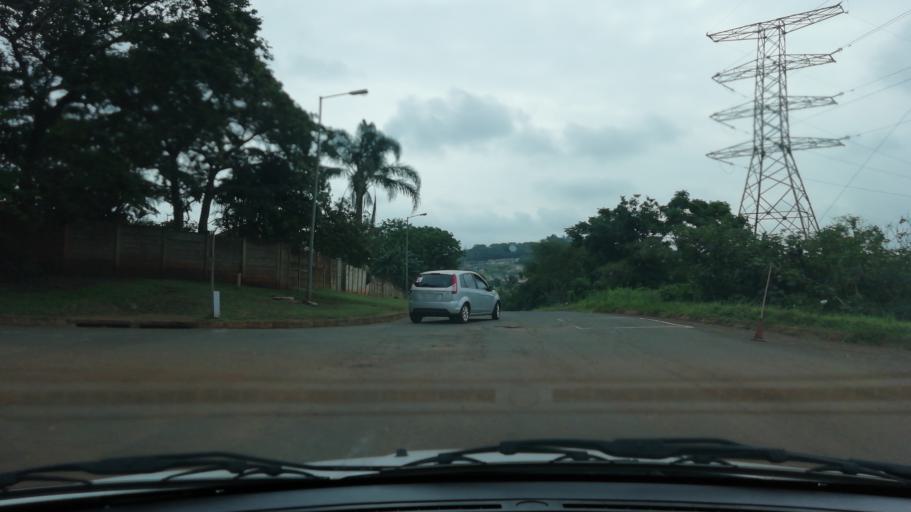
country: ZA
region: KwaZulu-Natal
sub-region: uThungulu District Municipality
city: Empangeni
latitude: -28.7381
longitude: 31.8874
